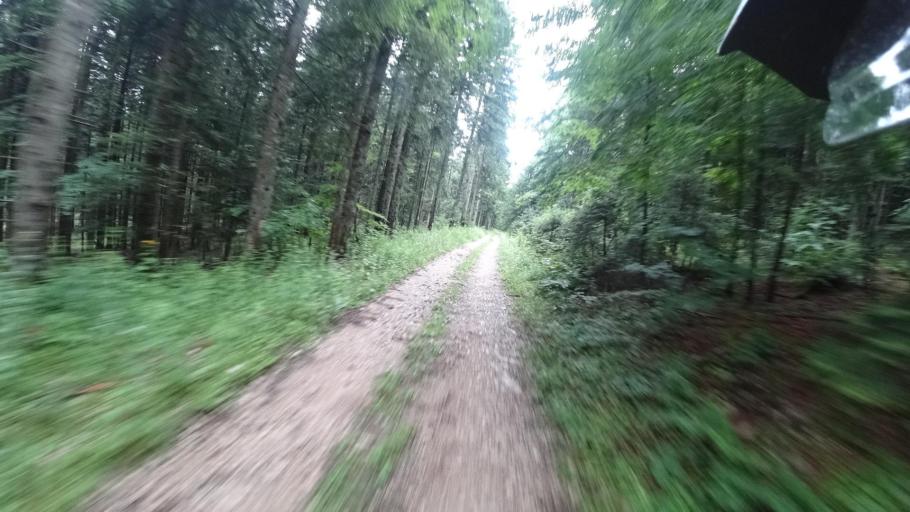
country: HR
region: Karlovacka
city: Plaski
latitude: 44.9446
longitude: 15.4076
